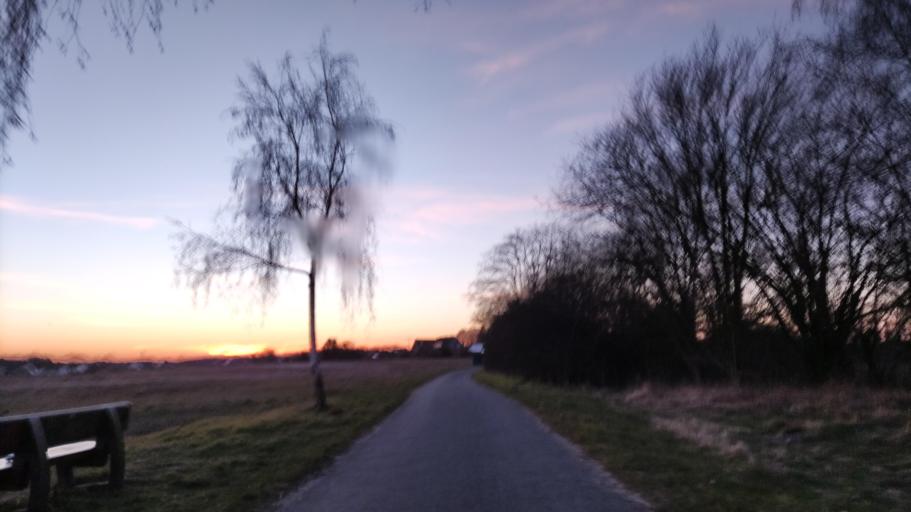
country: DE
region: Lower Saxony
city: Reppenstedt
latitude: 53.2458
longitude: 10.3727
